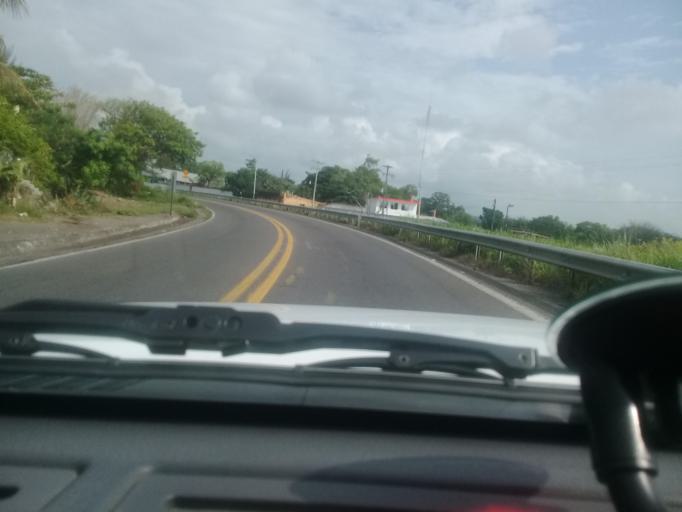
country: MX
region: Veracruz
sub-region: Paso de Ovejas
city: Tolome
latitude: 19.2646
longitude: -96.3738
